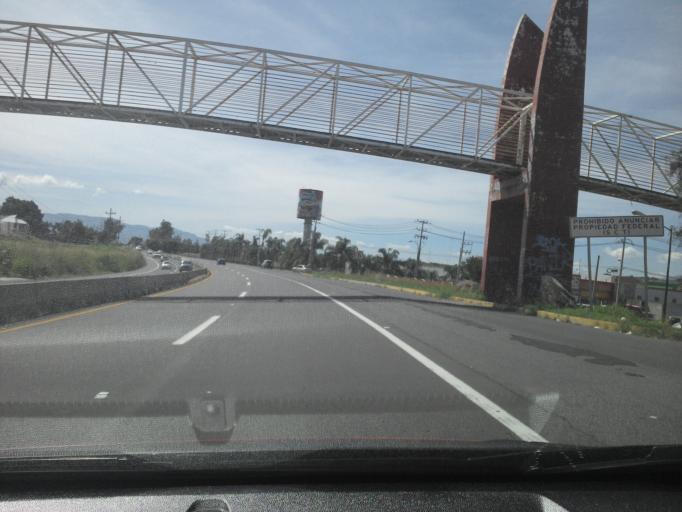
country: MX
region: Jalisco
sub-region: Tala
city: Los Ruisenores
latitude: 20.7035
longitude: -103.6874
